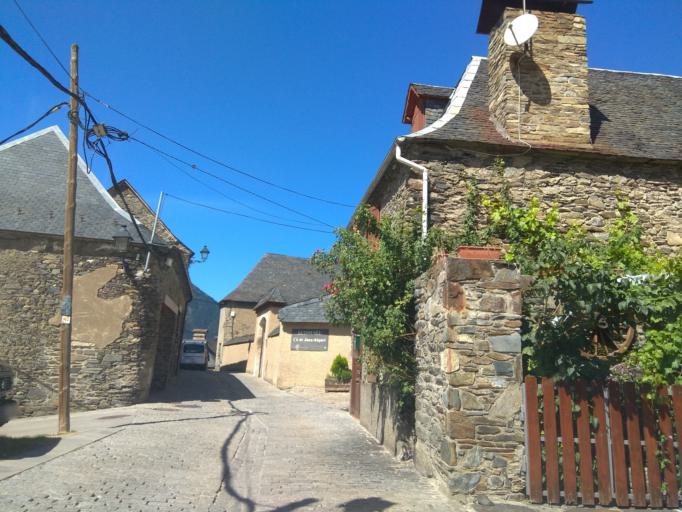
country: ES
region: Catalonia
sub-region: Provincia de Lleida
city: Les
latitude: 42.7479
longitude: 0.7260
